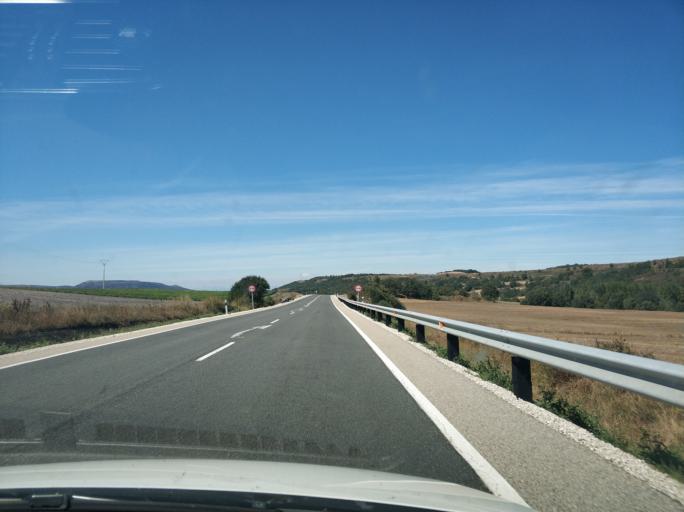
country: ES
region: Castille and Leon
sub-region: Provincia de Burgos
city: Basconcillos del Tozo
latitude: 42.6762
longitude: -3.9404
